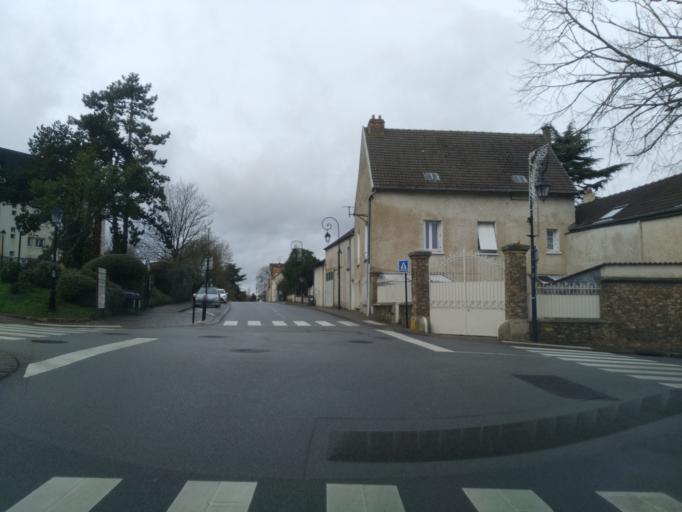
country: FR
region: Ile-de-France
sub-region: Departement des Yvelines
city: Chambourcy
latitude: 48.9034
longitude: 2.0453
